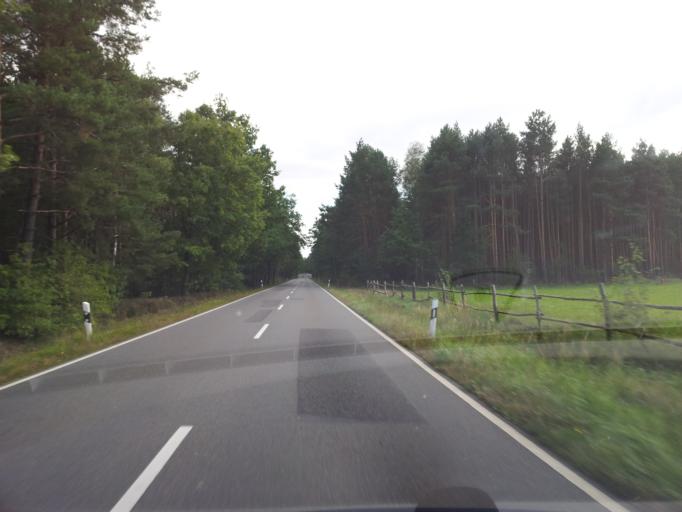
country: DE
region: Brandenburg
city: Finsterwalde
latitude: 51.6048
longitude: 13.7731
